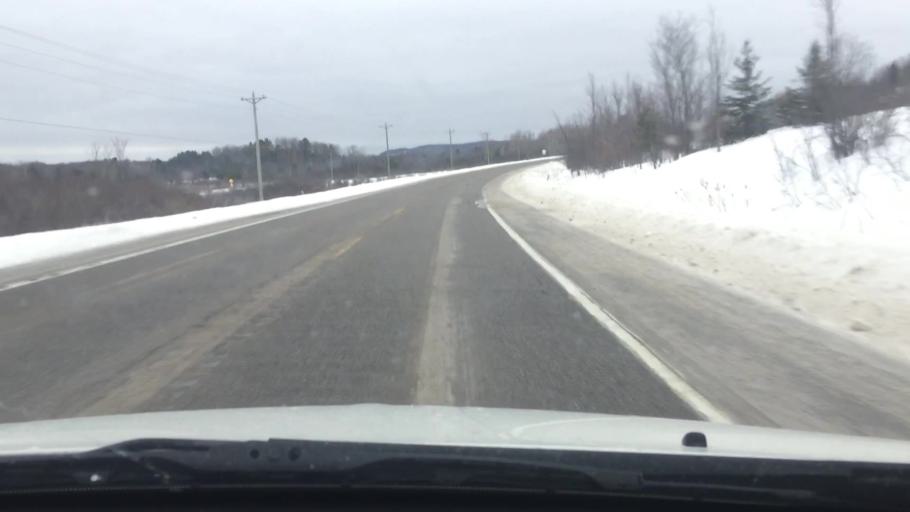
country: US
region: Michigan
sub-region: Charlevoix County
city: East Jordan
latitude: 45.1228
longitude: -85.1317
